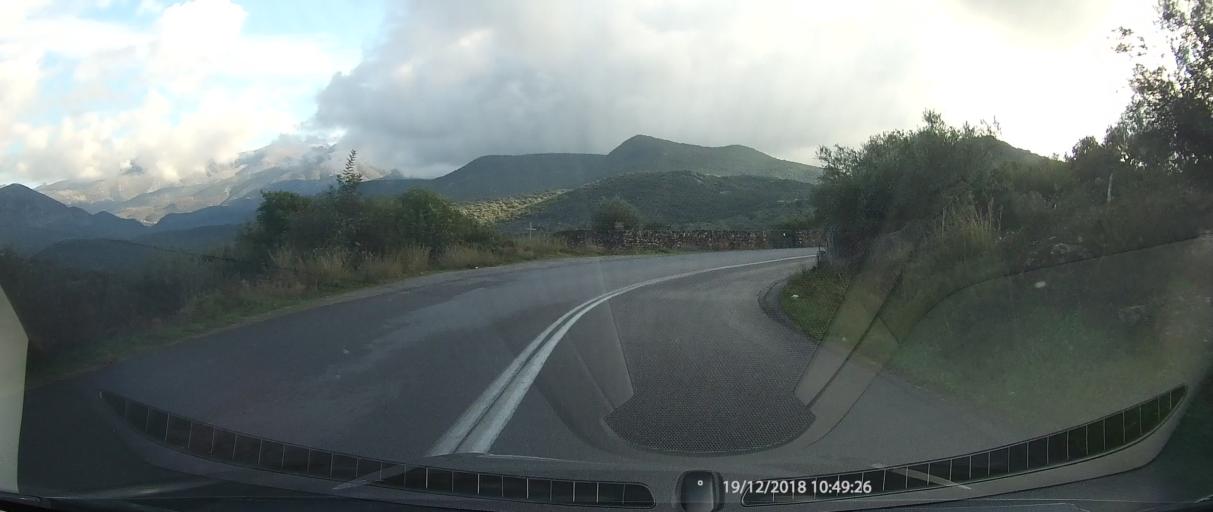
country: GR
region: Peloponnese
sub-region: Nomos Messinias
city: Kardamyli
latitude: 36.9264
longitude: 22.1996
